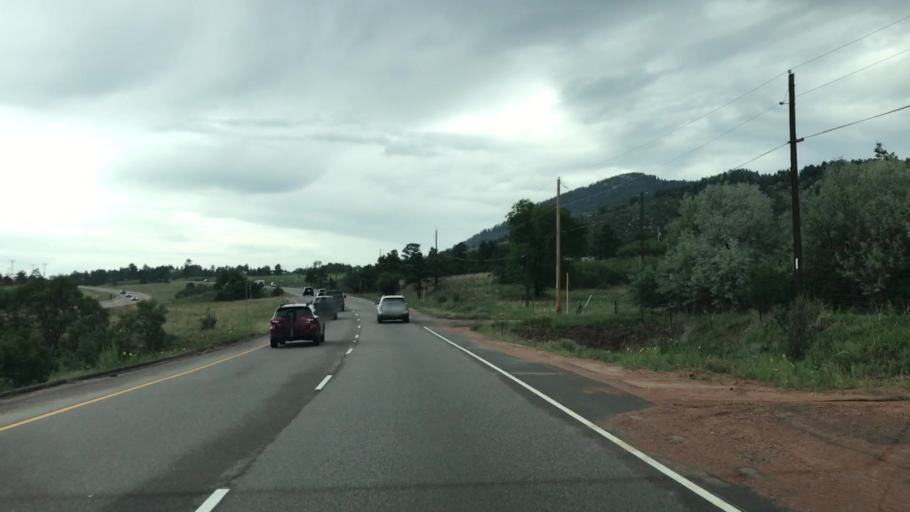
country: US
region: Colorado
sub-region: El Paso County
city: Cascade-Chipita Park
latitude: 38.9289
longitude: -104.9986
